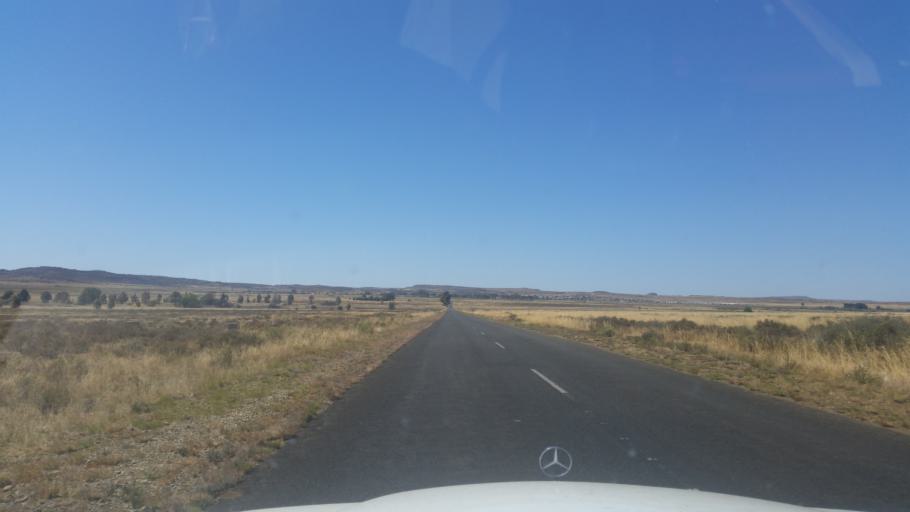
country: ZA
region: Eastern Cape
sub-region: Joe Gqabi District Municipality
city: Burgersdorp
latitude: -30.7524
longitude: 25.7698
